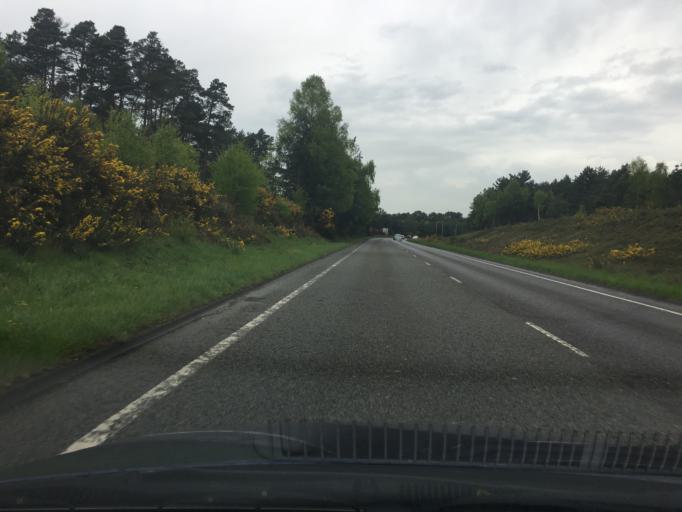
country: GB
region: England
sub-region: Bracknell Forest
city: Crowthorne
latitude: 51.3786
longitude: -0.7713
